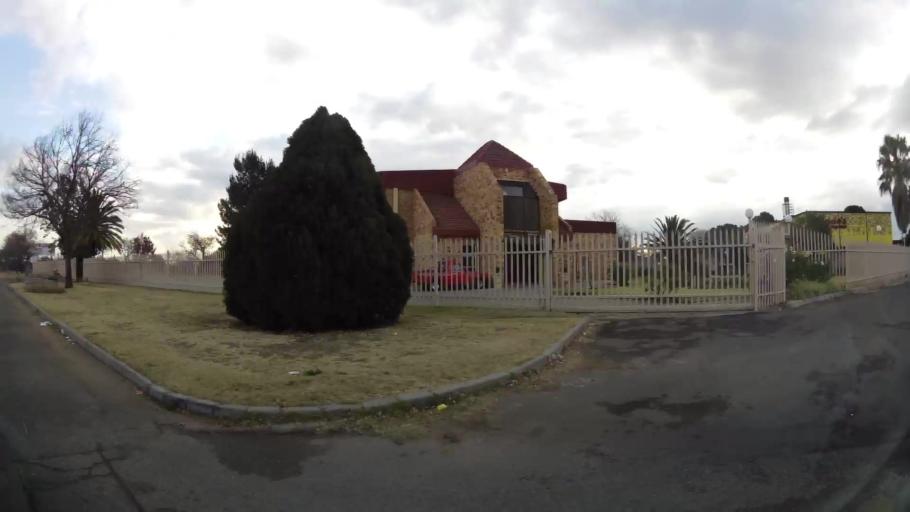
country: ZA
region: Orange Free State
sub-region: Lejweleputswa District Municipality
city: Welkom
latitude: -27.9788
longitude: 26.7317
